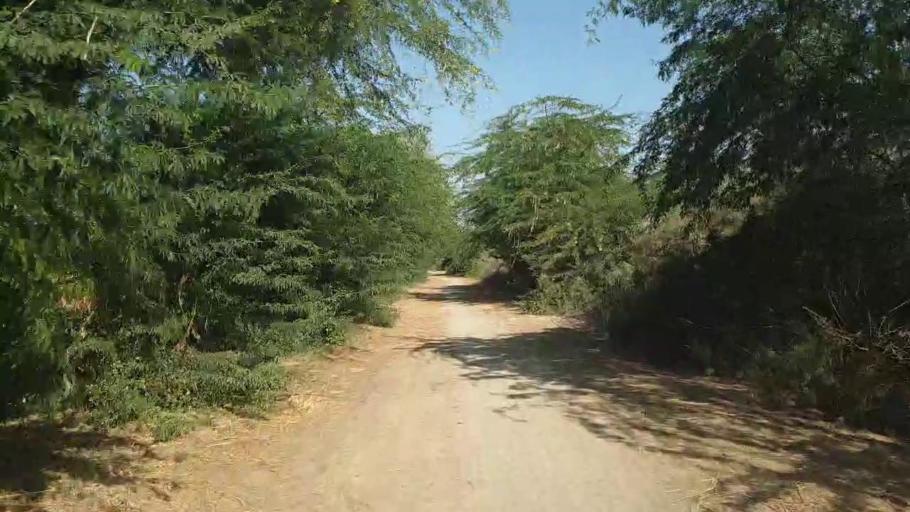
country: PK
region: Sindh
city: Talhar
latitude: 24.8175
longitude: 68.7838
